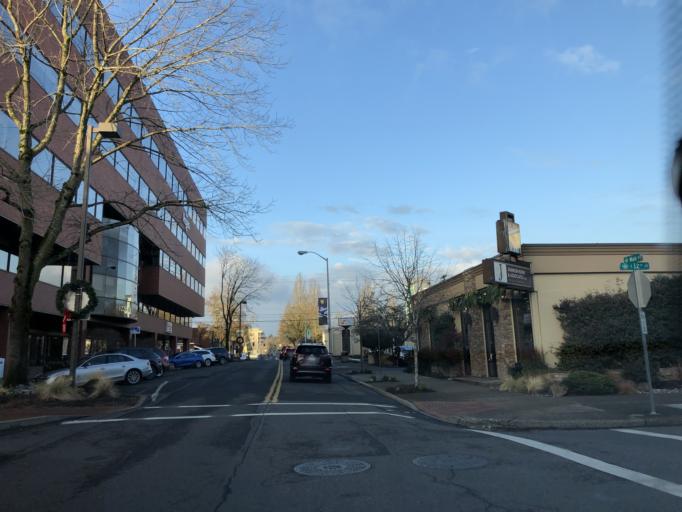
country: US
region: Washington
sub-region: Clark County
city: Vancouver
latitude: 45.6303
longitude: -122.6715
